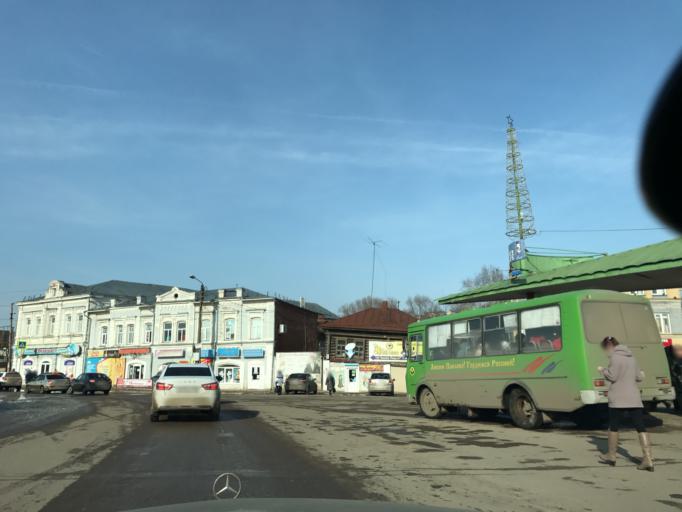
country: RU
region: Nizjnij Novgorod
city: Pavlovo
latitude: 55.9657
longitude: 43.0679
